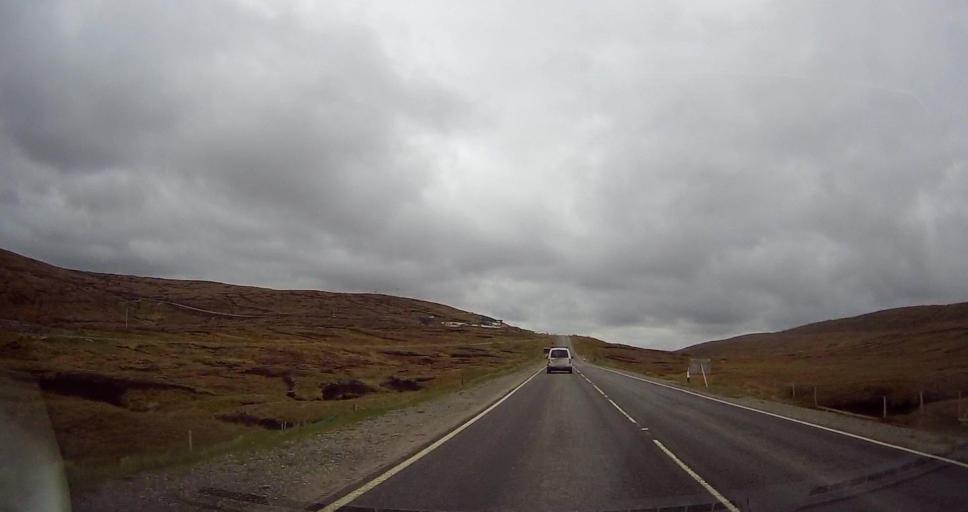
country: GB
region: Scotland
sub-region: Shetland Islands
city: Lerwick
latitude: 60.3296
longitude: -1.2538
